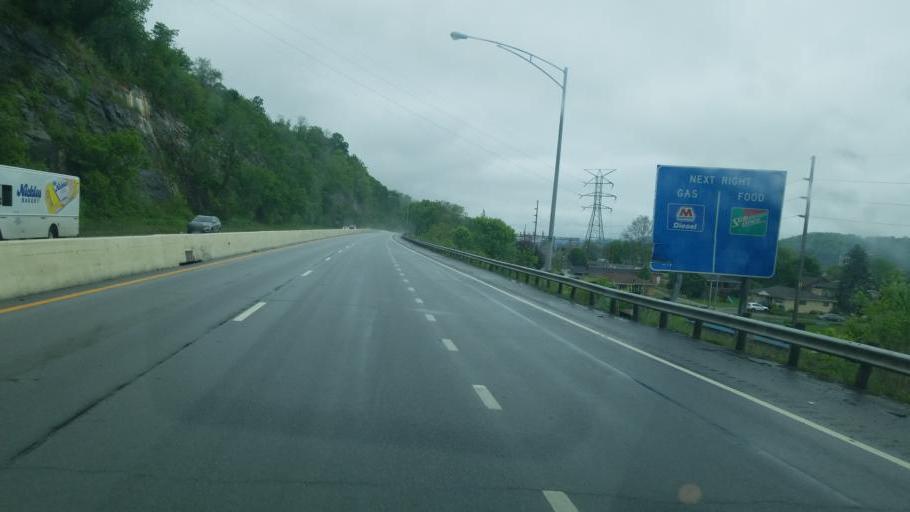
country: US
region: Ohio
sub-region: Jefferson County
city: Tiltonsville
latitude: 40.1635
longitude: -80.7074
